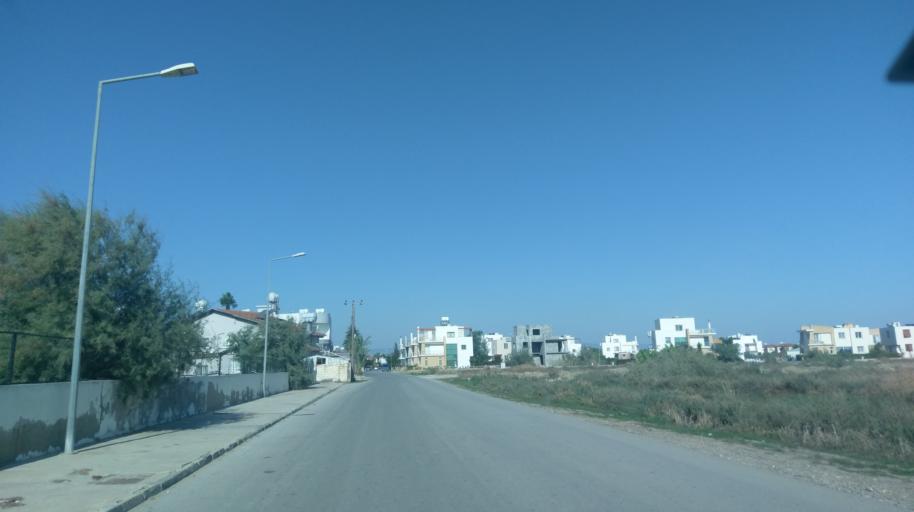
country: CY
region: Ammochostos
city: Acheritou
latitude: 35.1533
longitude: 33.8845
